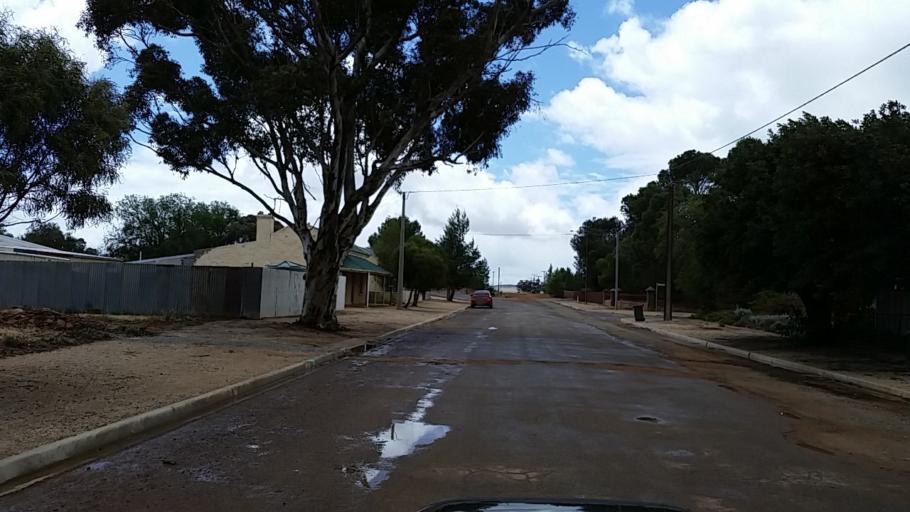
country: AU
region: South Australia
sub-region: Peterborough
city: Peterborough
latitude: -32.9742
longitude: 138.8416
